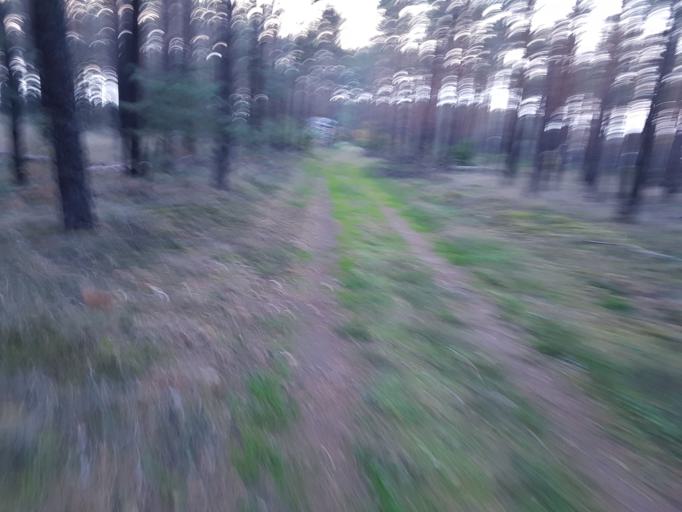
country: DE
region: Brandenburg
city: Bad Liebenwerda
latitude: 51.5426
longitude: 13.3809
